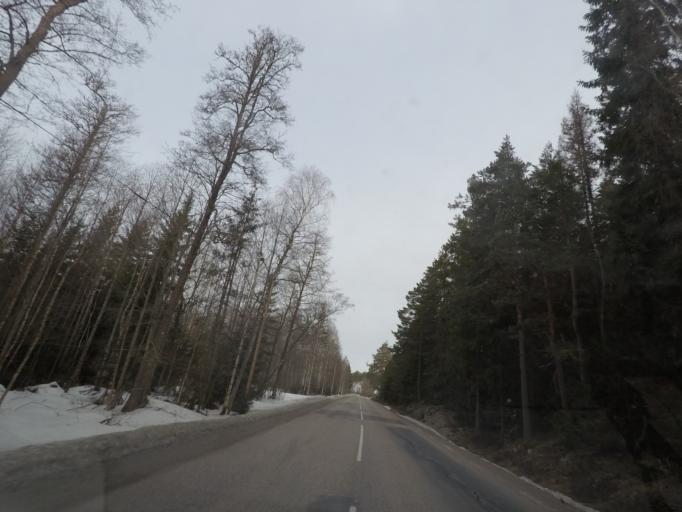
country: SE
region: Vaestmanland
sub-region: Vasteras
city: Skultuna
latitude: 59.7502
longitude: 16.3250
